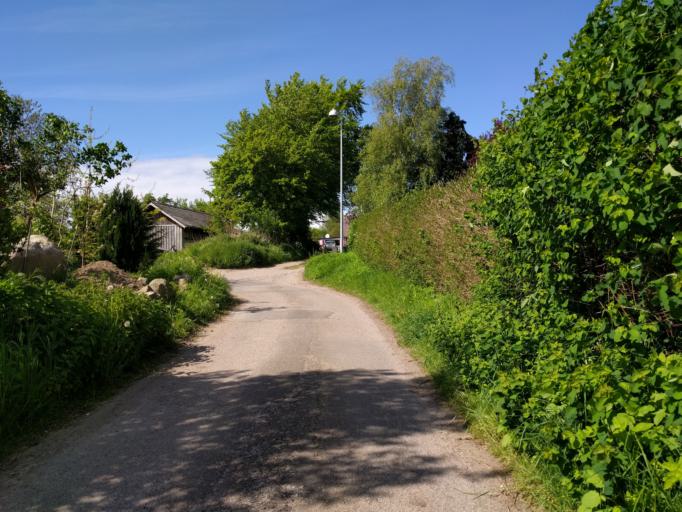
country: DK
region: Zealand
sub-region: Guldborgsund Kommune
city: Stubbekobing
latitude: 54.9172
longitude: 12.0507
